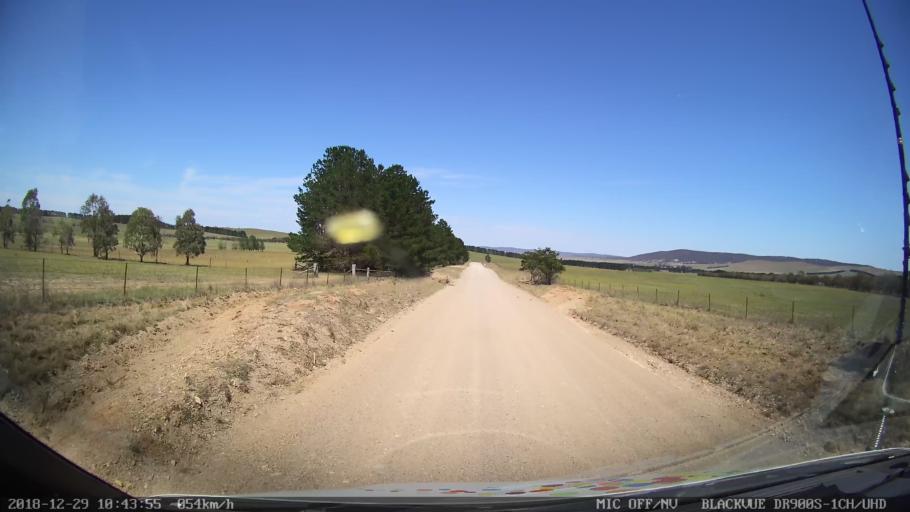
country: AU
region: New South Wales
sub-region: Palerang
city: Bungendore
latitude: -35.0411
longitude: 149.5336
